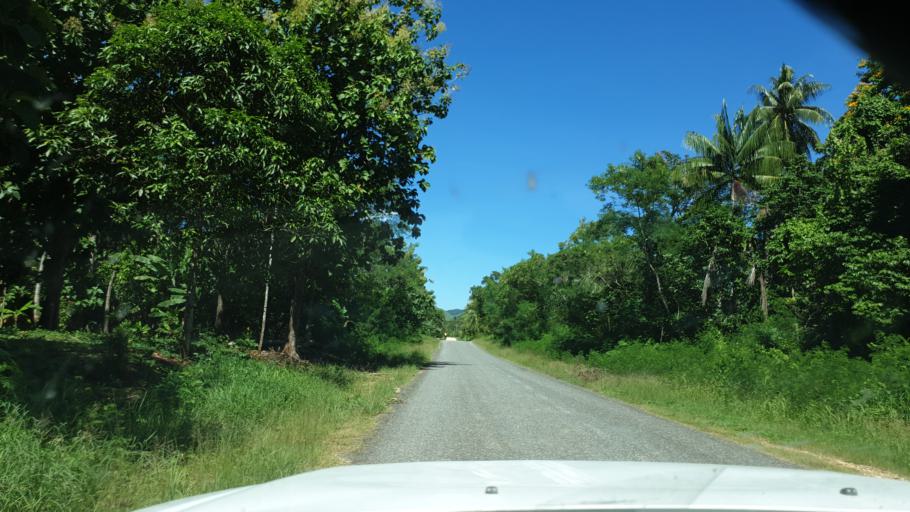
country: PG
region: Madang
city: Madang
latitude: -4.4533
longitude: 145.3810
